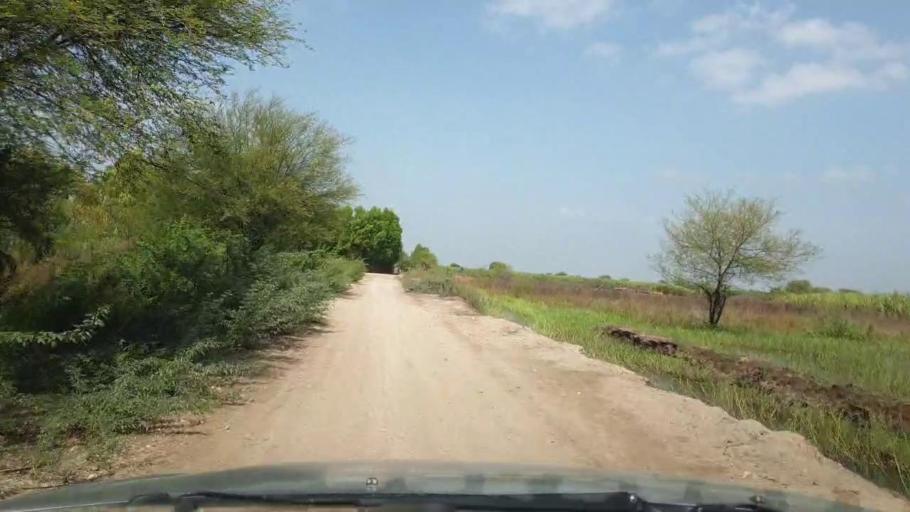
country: PK
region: Sindh
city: Rajo Khanani
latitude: 25.0314
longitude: 68.9165
